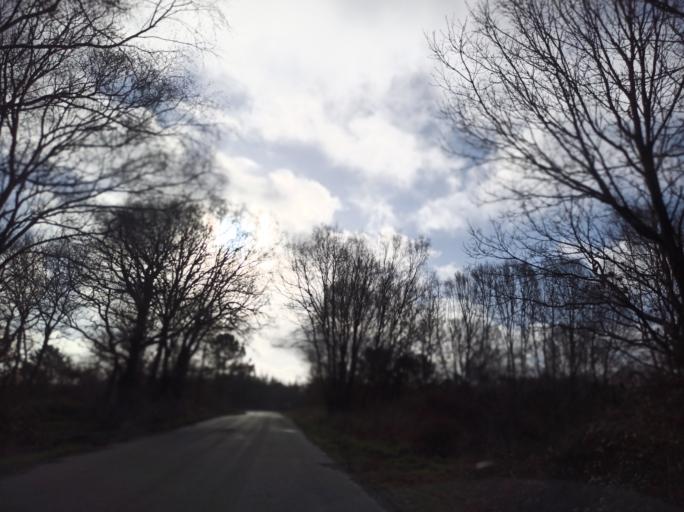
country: ES
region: Galicia
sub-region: Provincia da Coruna
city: Sobrado
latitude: 43.0932
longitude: -7.9735
